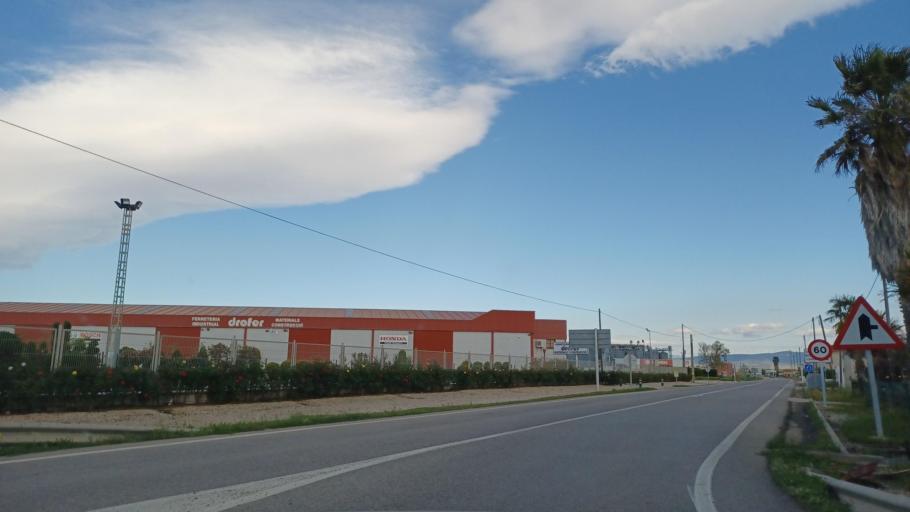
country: ES
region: Catalonia
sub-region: Provincia de Tarragona
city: Deltebre
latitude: 40.7301
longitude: 0.7104
